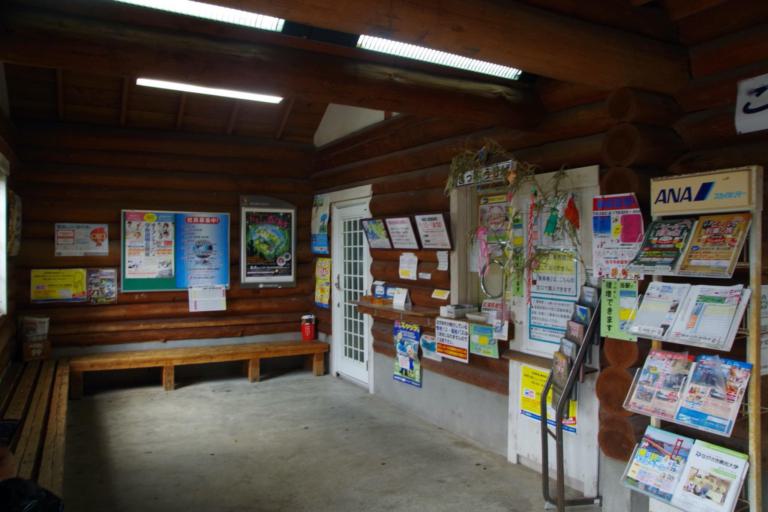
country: JP
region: Nagasaki
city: Sasebo
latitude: 33.2368
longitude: 129.6472
